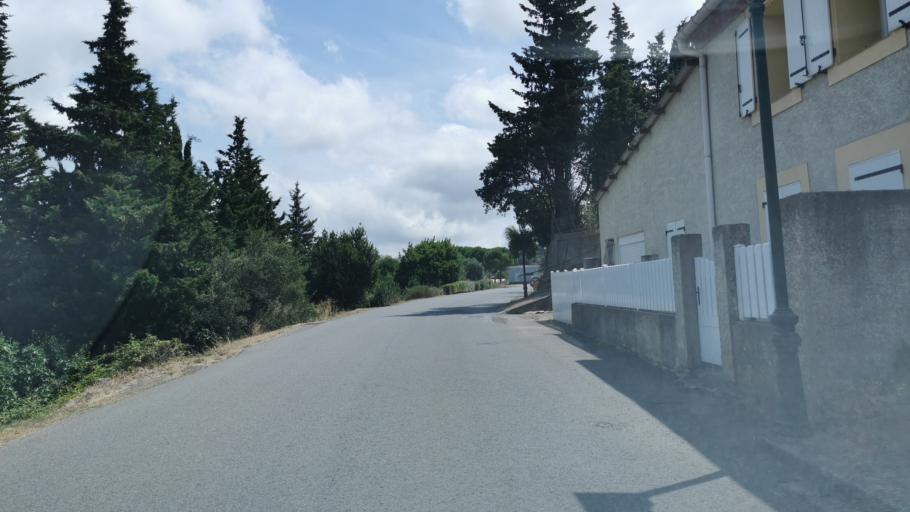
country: FR
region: Languedoc-Roussillon
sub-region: Departement de l'Aude
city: Bizanet
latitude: 43.1665
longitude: 2.8754
